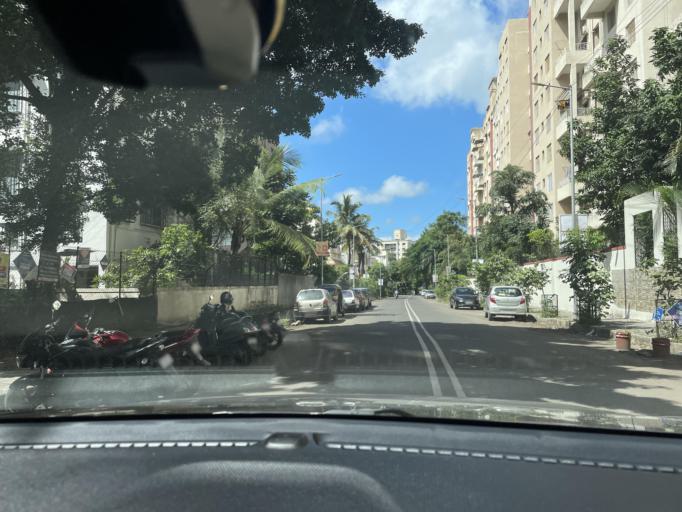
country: IN
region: Maharashtra
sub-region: Pune Division
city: Kharakvasla
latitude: 18.5131
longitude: 73.7773
